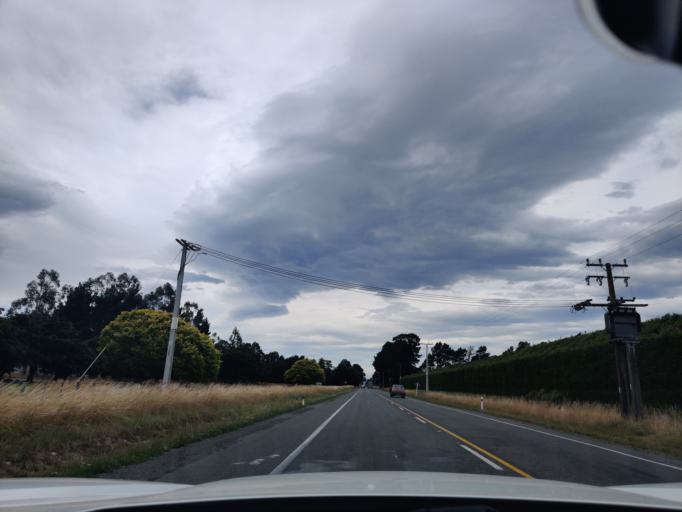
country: NZ
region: Wellington
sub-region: Masterton District
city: Masterton
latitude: -40.9875
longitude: 175.5755
